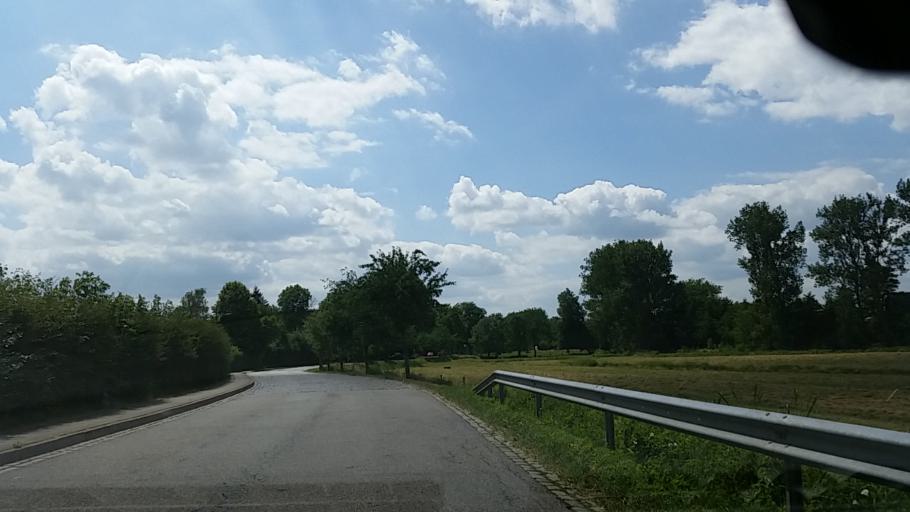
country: DE
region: Schleswig-Holstein
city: Oststeinbek
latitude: 53.5041
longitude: 10.1557
